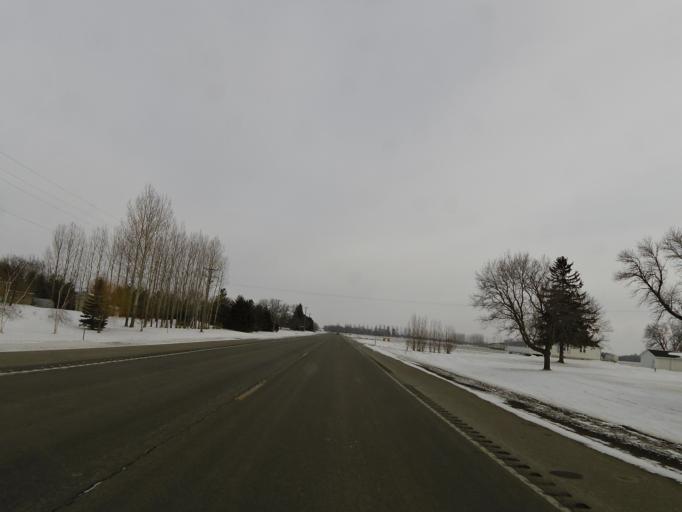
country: US
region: Minnesota
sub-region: McLeod County
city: Lester Prairie
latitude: 44.9062
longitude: -94.0866
